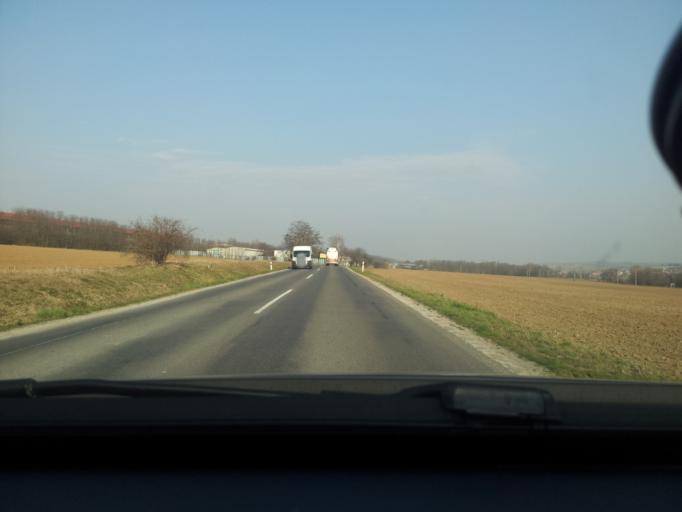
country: SK
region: Trnavsky
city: Hlohovec
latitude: 48.3758
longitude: 17.8804
